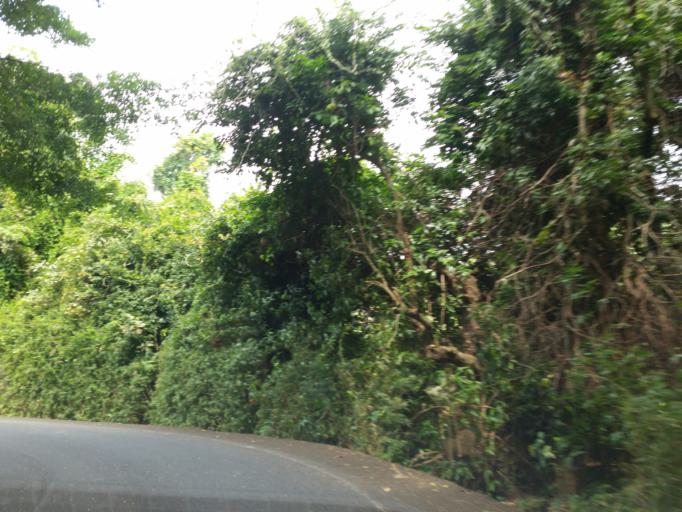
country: RE
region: Reunion
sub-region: Reunion
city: Sainte-Suzanne
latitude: -20.9194
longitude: 55.6196
